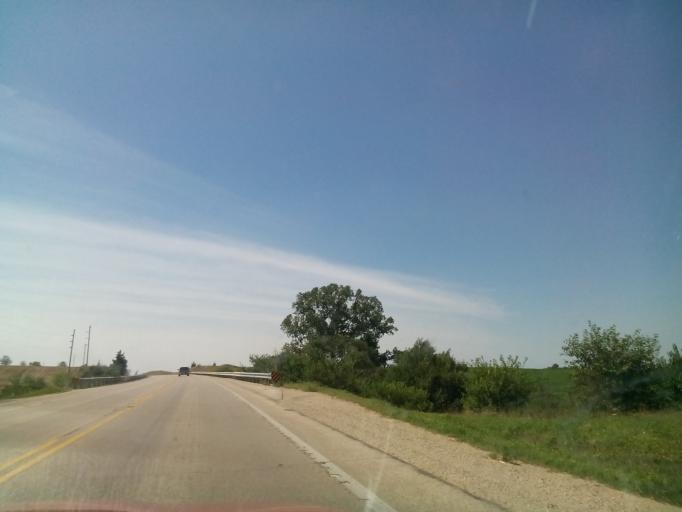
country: US
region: Wisconsin
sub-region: Green County
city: Monroe
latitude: 42.6556
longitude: -89.6290
